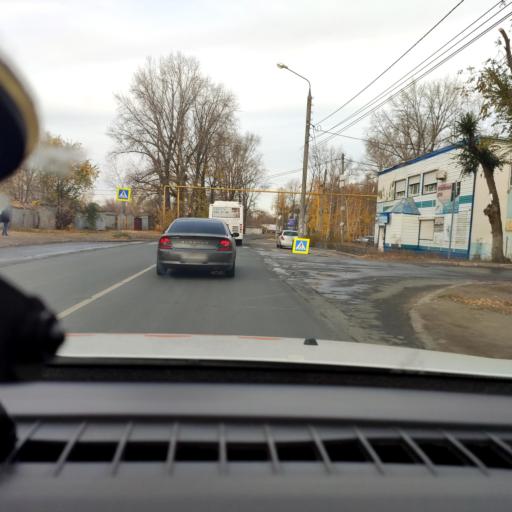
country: RU
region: Samara
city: Rozhdestveno
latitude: 53.1435
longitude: 50.0374
